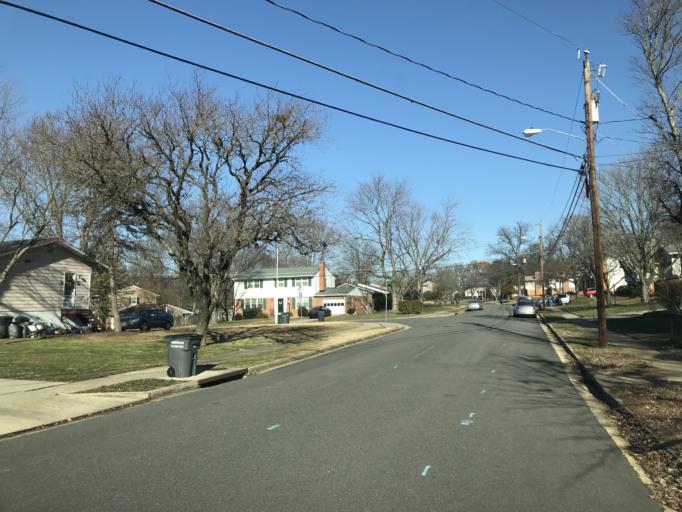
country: US
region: Virginia
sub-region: Fairfax County
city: Franconia
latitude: 38.7854
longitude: -77.1668
